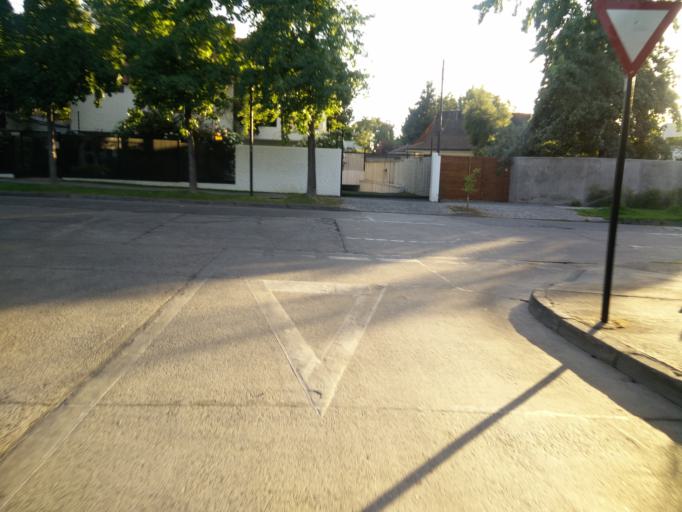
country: CL
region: Santiago Metropolitan
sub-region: Provincia de Santiago
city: Villa Presidente Frei, Nunoa, Santiago, Chile
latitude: -33.3871
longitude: -70.5810
